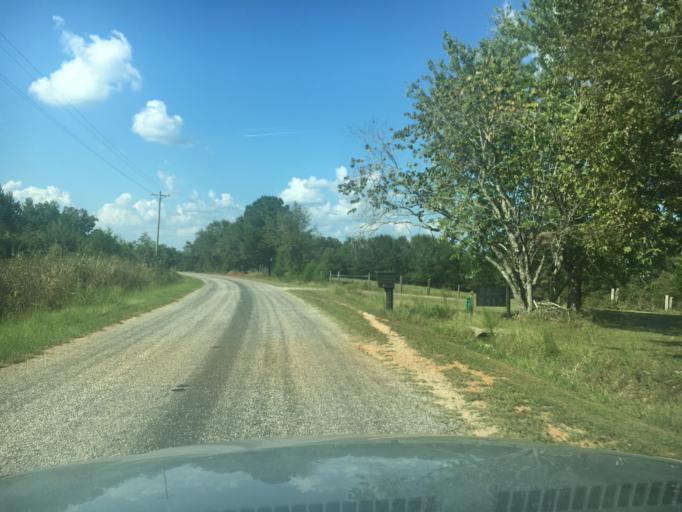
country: US
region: South Carolina
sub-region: Greenwood County
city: Ware Shoals
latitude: 34.4906
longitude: -82.2301
